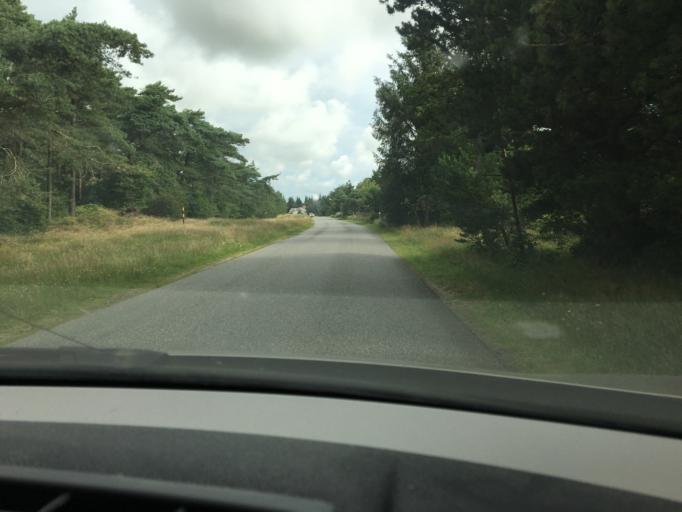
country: DK
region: Central Jutland
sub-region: Ringkobing-Skjern Kommune
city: Hvide Sande
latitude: 55.8224
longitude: 8.2158
